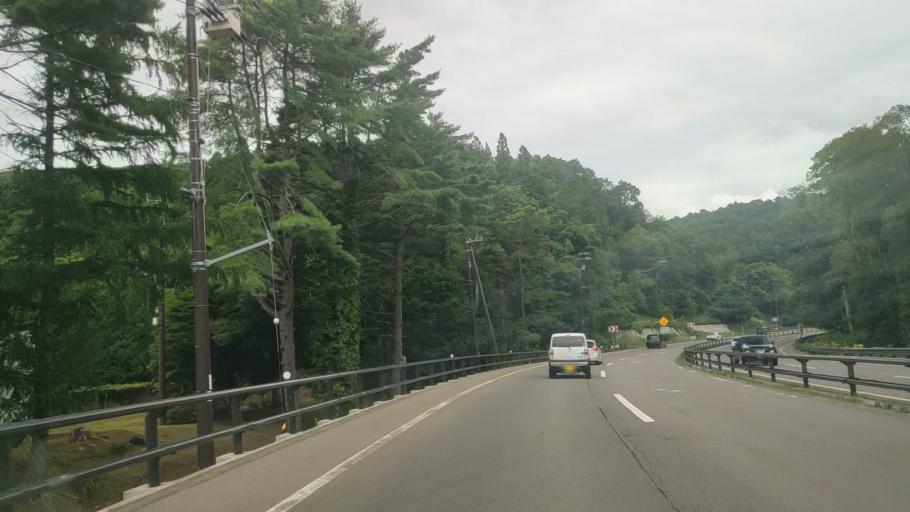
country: JP
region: Hokkaido
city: Nanae
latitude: 41.9618
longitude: 140.6472
